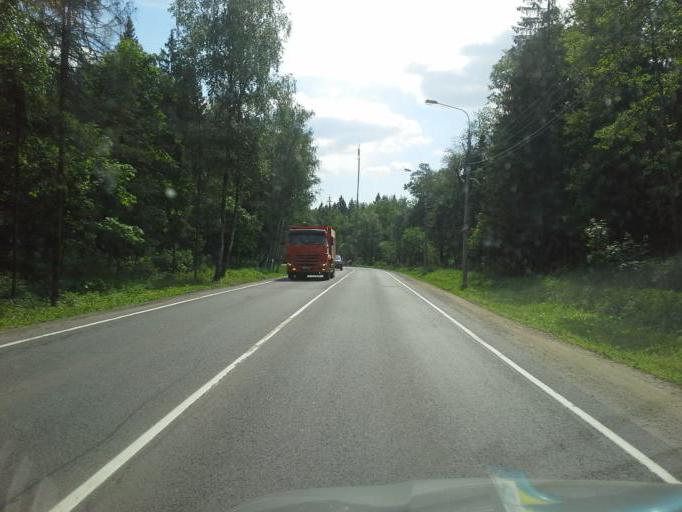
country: RU
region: Moskovskaya
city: Odintsovo
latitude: 55.7027
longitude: 37.2680
